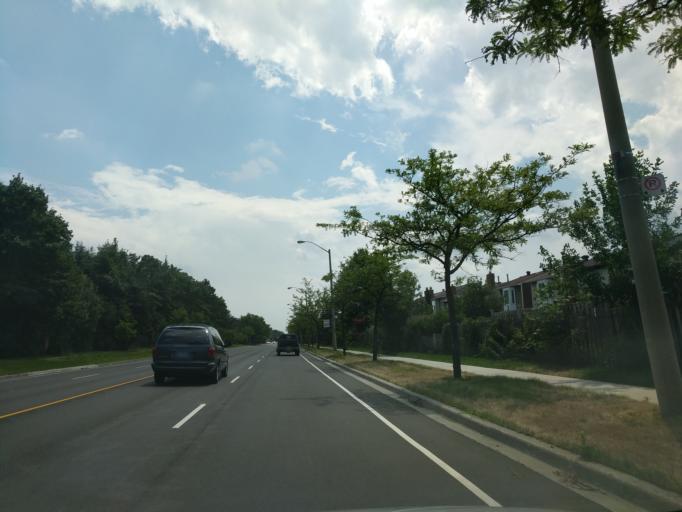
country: CA
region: Ontario
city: Markham
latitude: 43.8203
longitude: -79.3164
